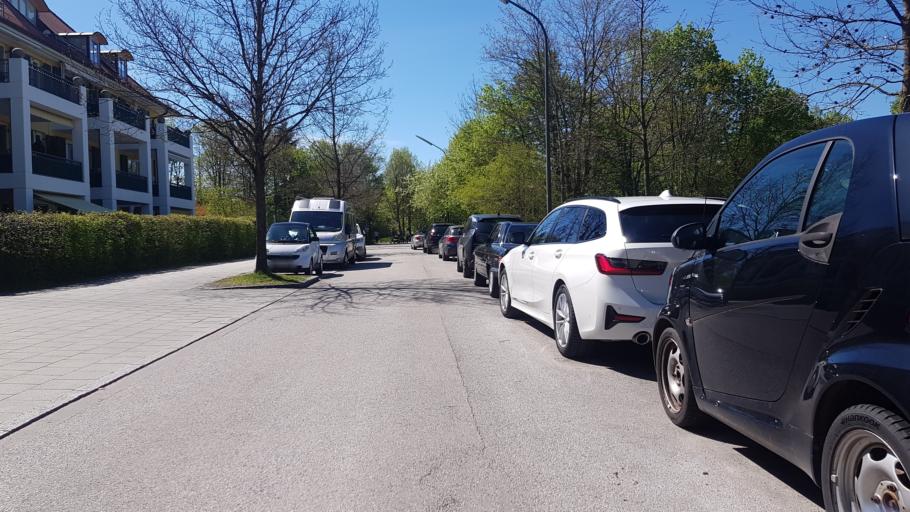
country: DE
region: Bavaria
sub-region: Upper Bavaria
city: Pasing
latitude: 48.1706
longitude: 11.5017
